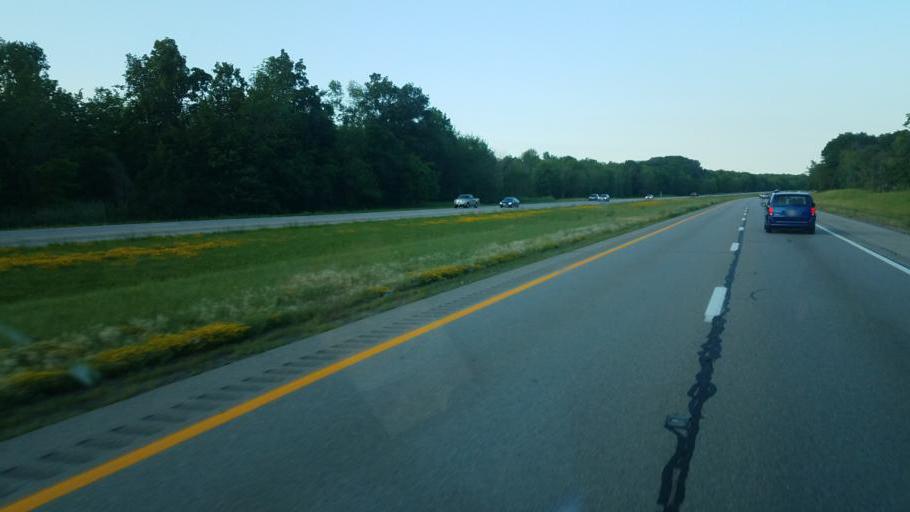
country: US
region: Ohio
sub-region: Lake County
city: Madison
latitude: 41.7659
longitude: -80.9921
